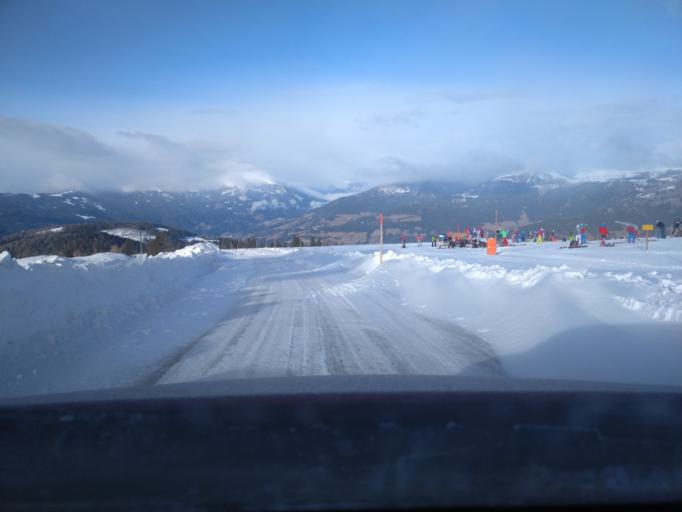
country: AT
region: Carinthia
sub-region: Politischer Bezirk Villach Land
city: Arriach
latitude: 46.6964
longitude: 13.9108
